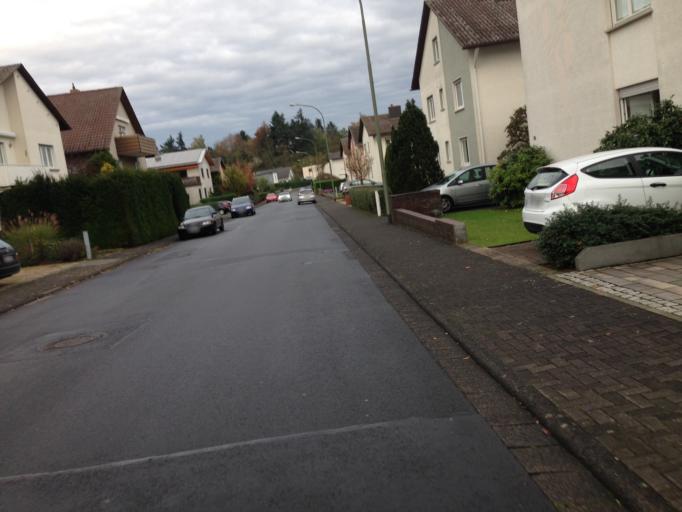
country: DE
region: Hesse
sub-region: Regierungsbezirk Giessen
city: Heuchelheim
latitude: 50.5861
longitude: 8.6288
